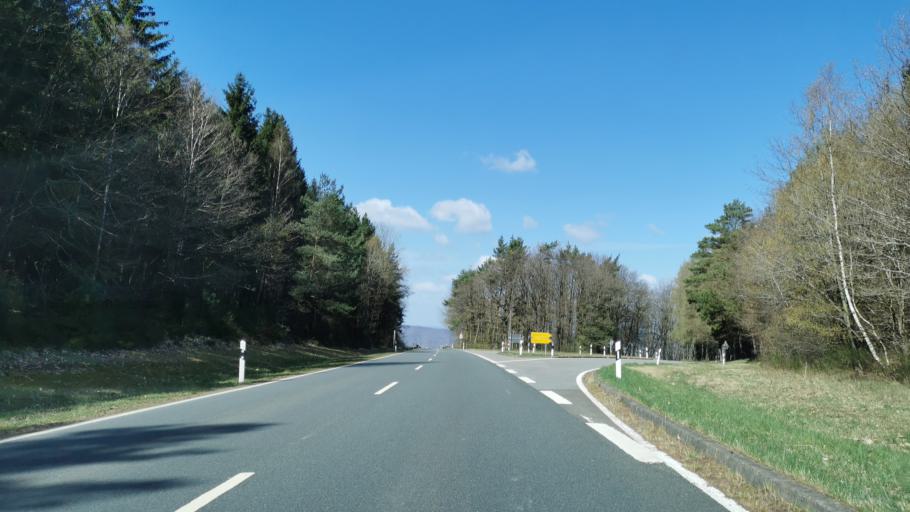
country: DE
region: Rheinland-Pfalz
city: Horath
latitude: 49.8481
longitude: 6.9783
